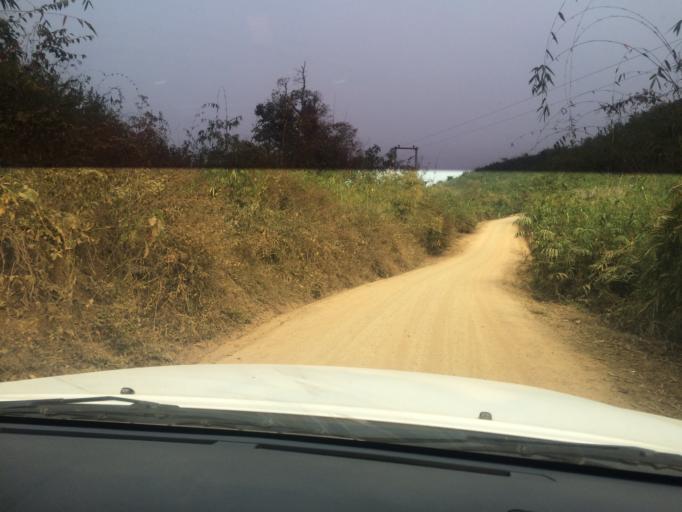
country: LA
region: Loungnamtha
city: Muang Nale
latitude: 20.4360
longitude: 101.7128
